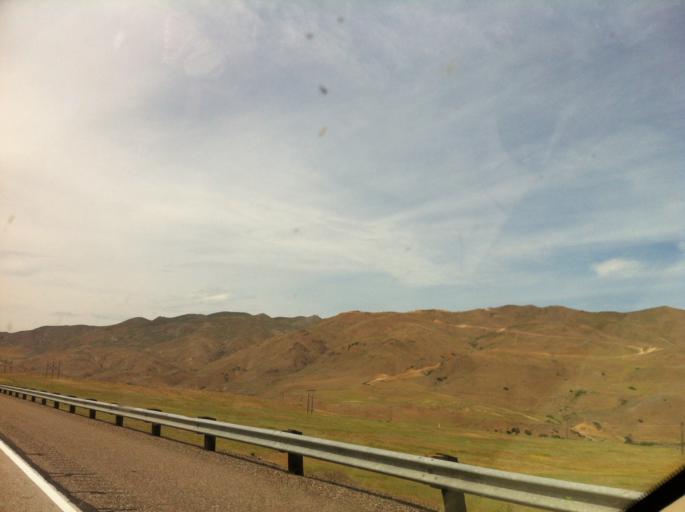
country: US
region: Idaho
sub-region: Washington County
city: Weiser
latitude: 44.3544
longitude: -117.2903
